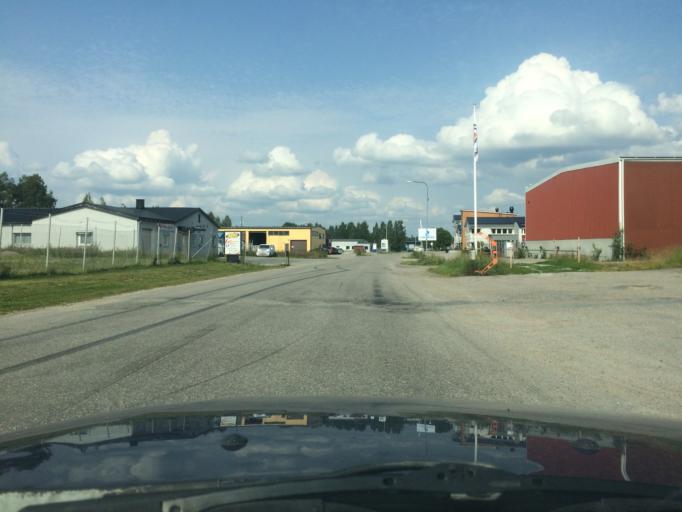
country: SE
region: Norrbotten
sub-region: Pitea Kommun
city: Bergsviken
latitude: 65.3363
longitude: 21.4159
